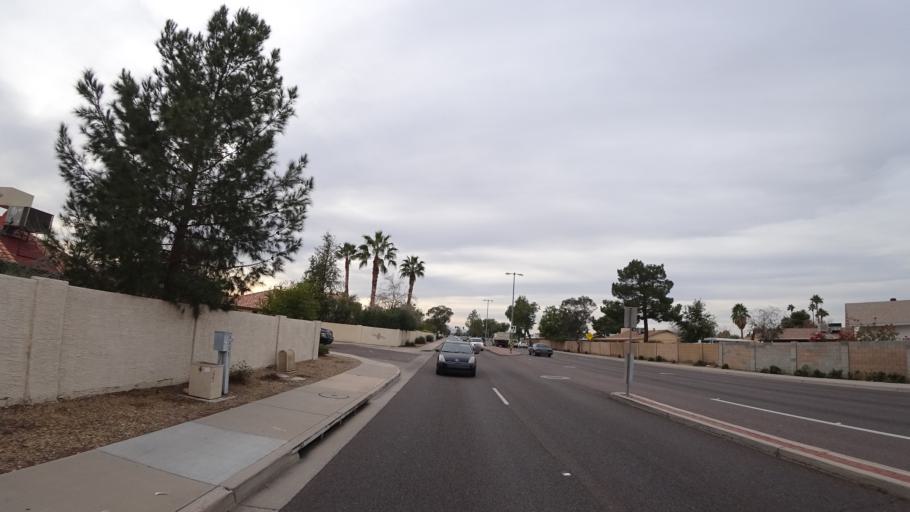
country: US
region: Arizona
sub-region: Maricopa County
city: Glendale
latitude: 33.5819
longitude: -112.1753
